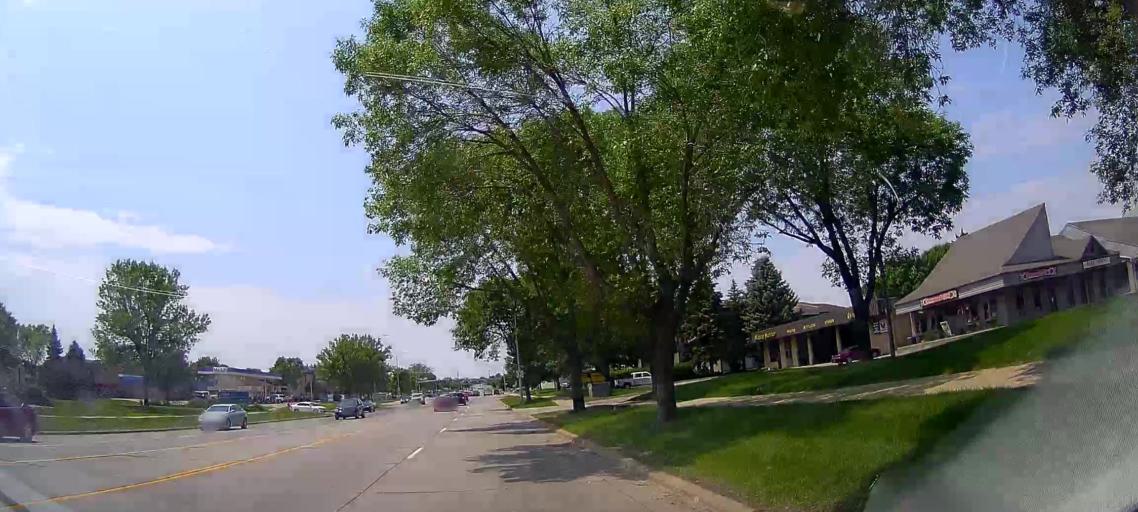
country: US
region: South Dakota
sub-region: Minnehaha County
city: Sioux Falls
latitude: 43.5077
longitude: -96.7679
